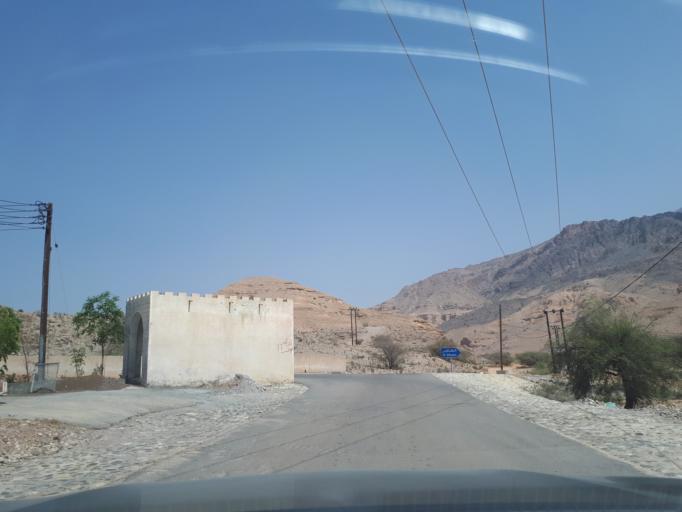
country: OM
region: Ash Sharqiyah
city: Ibra'
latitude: 23.0806
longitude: 58.8716
